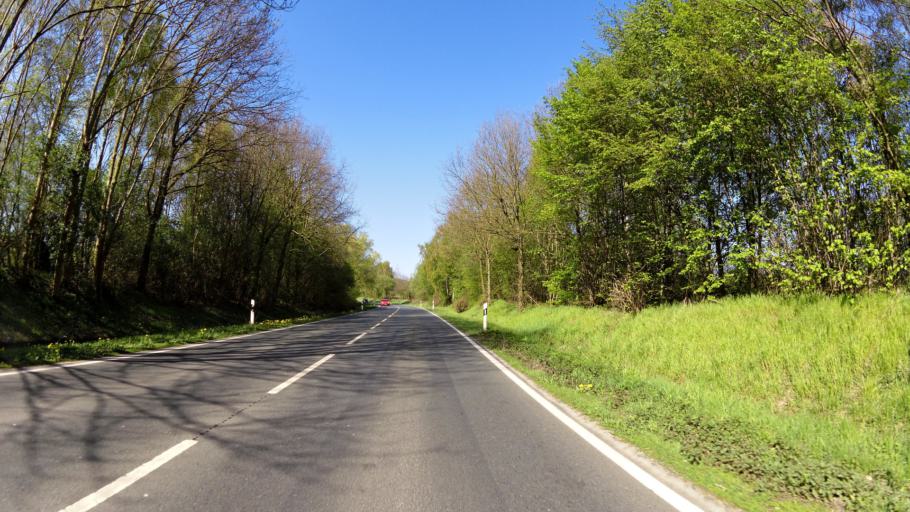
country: DE
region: Lower Saxony
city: Syke
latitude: 52.9254
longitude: 8.8136
